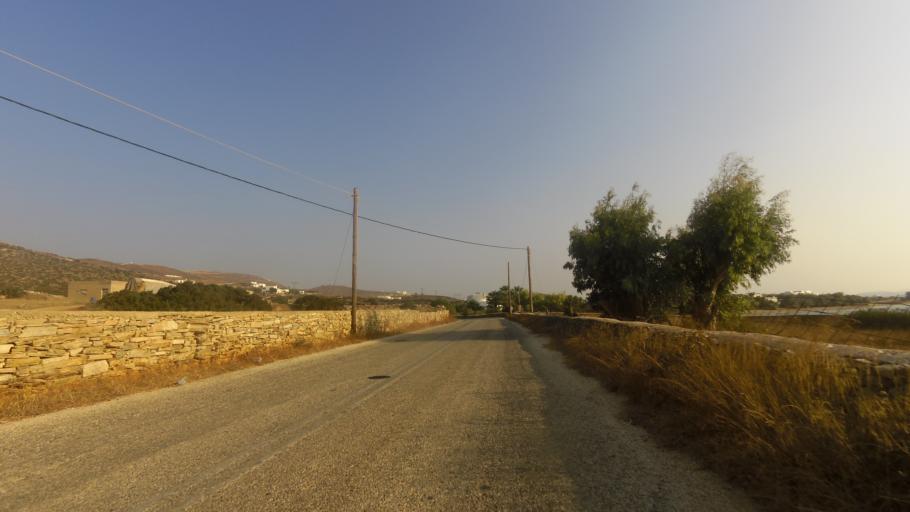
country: GR
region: South Aegean
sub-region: Nomos Kykladon
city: Antiparos
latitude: 37.0225
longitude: 25.0770
